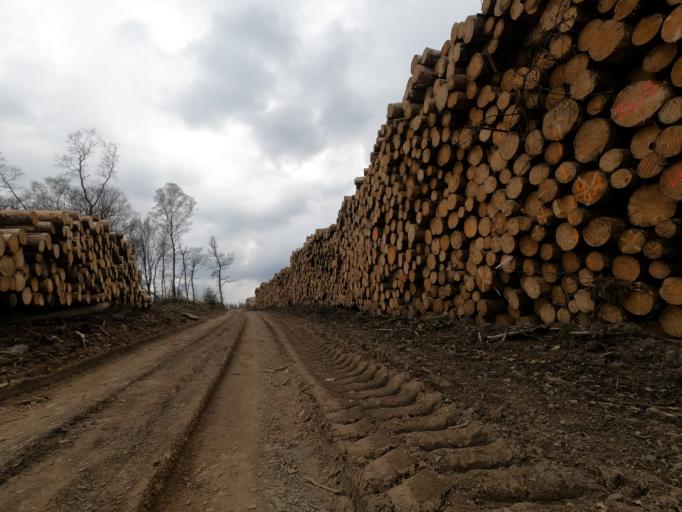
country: DE
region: North Rhine-Westphalia
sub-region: Regierungsbezirk Arnsberg
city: Herscheid
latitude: 51.1678
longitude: 7.7389
